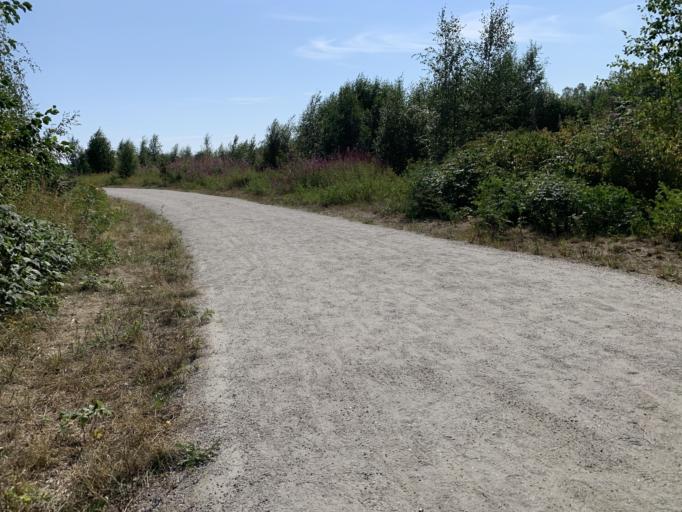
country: SE
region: Vaesternorrland
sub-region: Timra Kommun
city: Soraker
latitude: 62.5150
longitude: 17.4499
